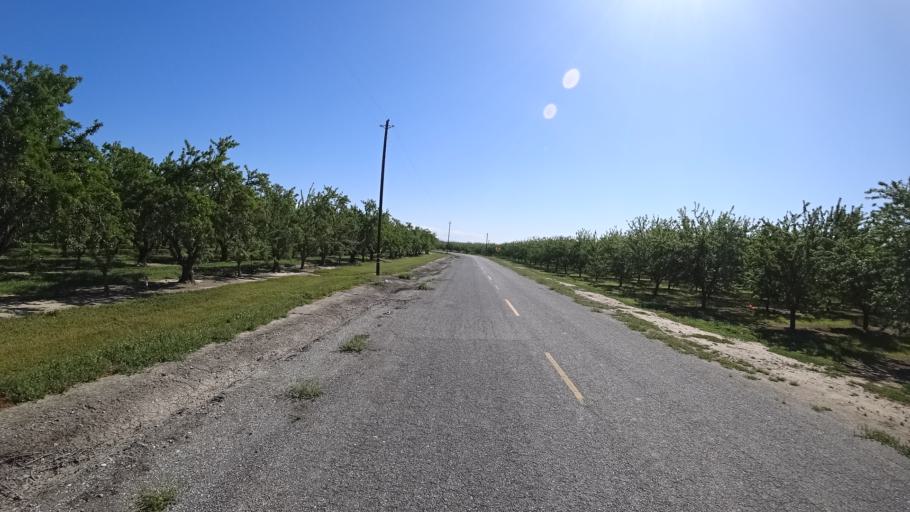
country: US
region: California
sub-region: Glenn County
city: Hamilton City
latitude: 39.7286
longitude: -122.0177
